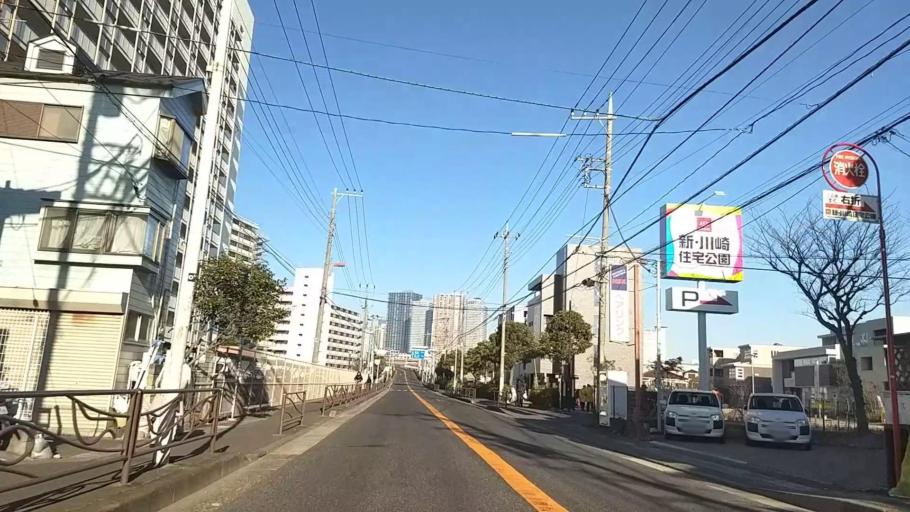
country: JP
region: Kanagawa
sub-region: Kawasaki-shi
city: Kawasaki
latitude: 35.5616
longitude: 139.6691
